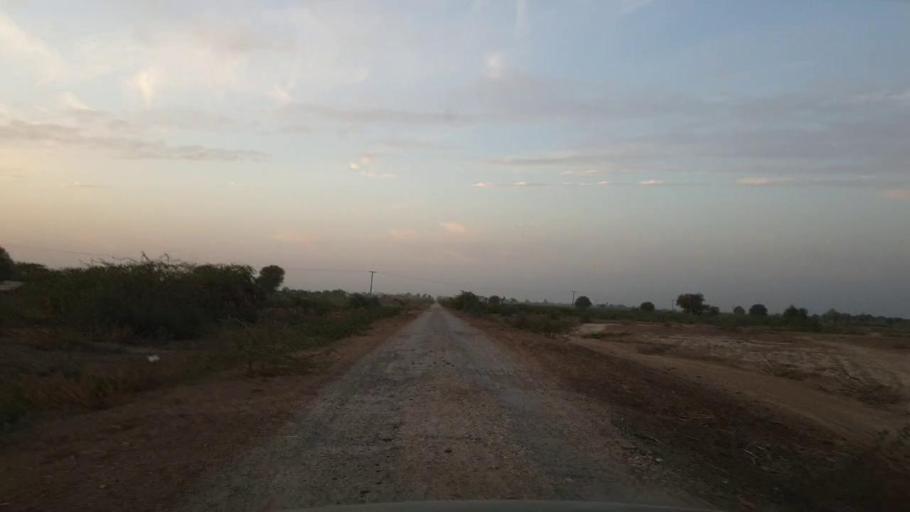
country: PK
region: Sindh
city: Kunri
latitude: 25.1336
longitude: 69.5641
